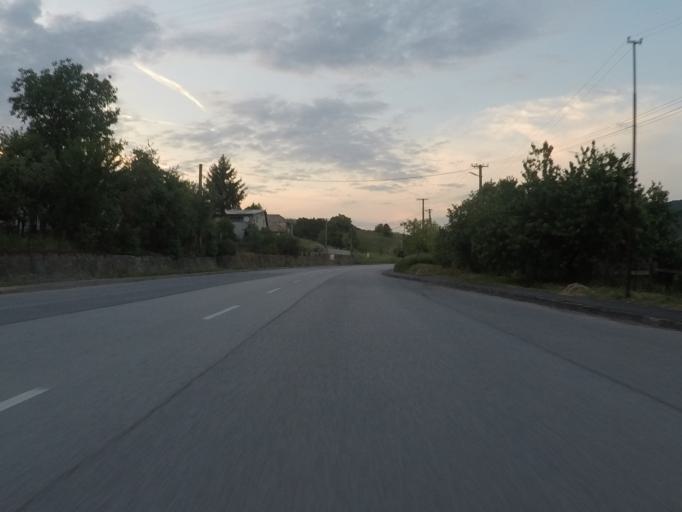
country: SK
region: Banskobystricky
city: Rimavska Sobota
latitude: 48.4796
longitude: 19.9445
